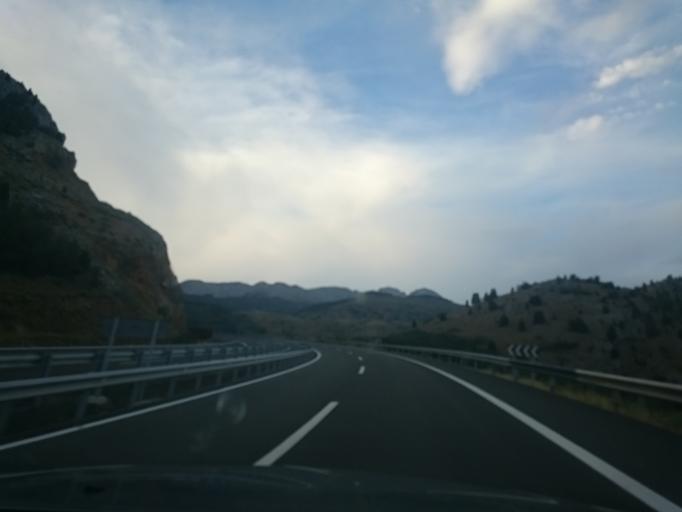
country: ES
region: Castille and Leon
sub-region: Provincia de Leon
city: Sena de Luna
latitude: 42.8759
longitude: -5.8817
